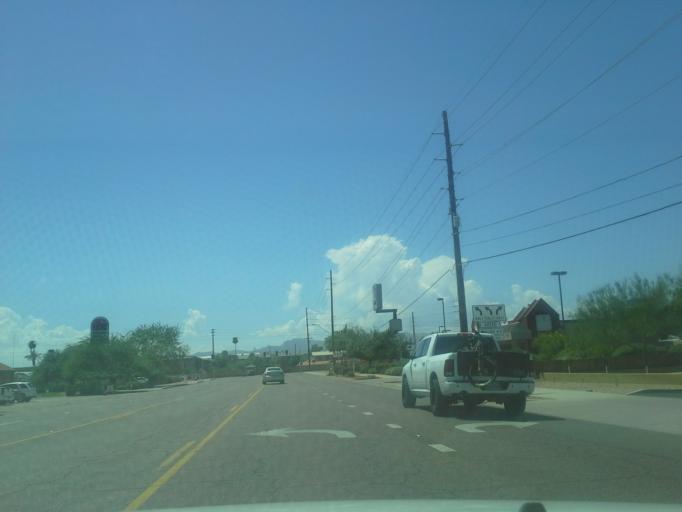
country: US
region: Arizona
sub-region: Maricopa County
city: Litchfield Park
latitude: 33.5370
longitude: -112.3563
